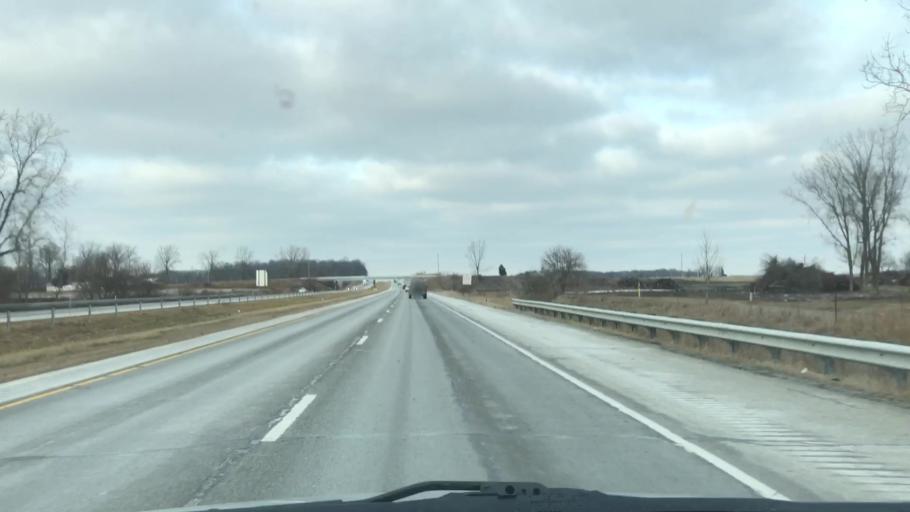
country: US
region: Indiana
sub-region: DeKalb County
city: Waterloo
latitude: 41.5377
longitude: -85.0557
